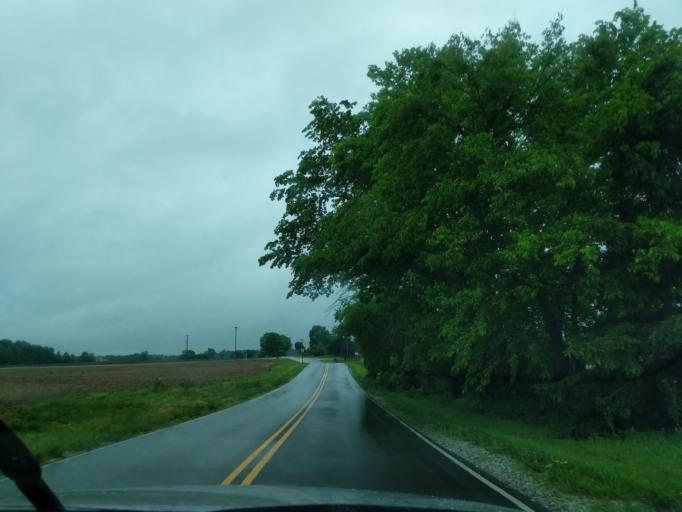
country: US
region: Indiana
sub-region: Madison County
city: Lapel
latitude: 40.0669
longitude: -85.8986
